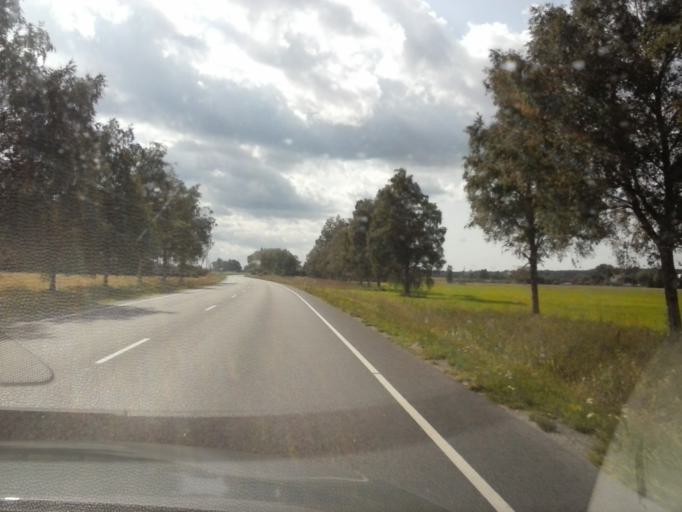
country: EE
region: Jaervamaa
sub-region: Tueri vald
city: Sarevere
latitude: 58.7574
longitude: 25.3616
